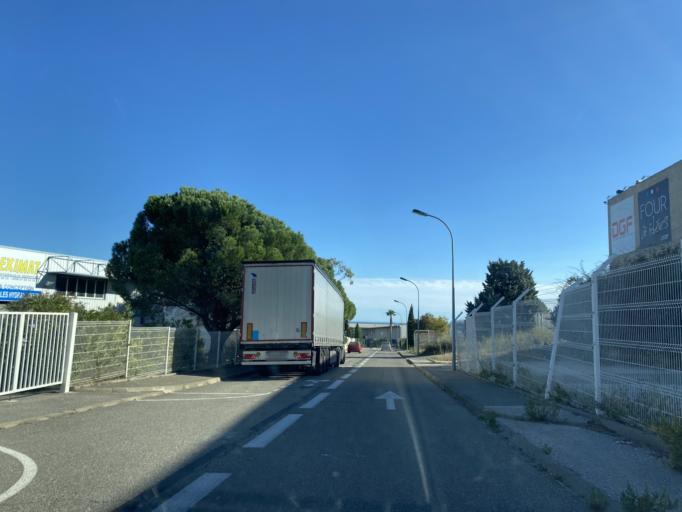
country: FR
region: Provence-Alpes-Cote d'Azur
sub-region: Departement des Bouches-du-Rhone
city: Ceyreste
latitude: 43.2072
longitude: 5.6067
